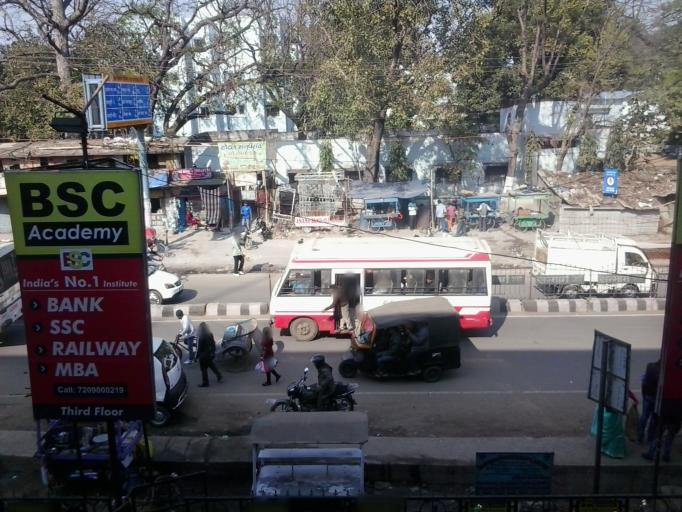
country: IN
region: Jharkhand
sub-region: Ranchi
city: Ranchi
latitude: 23.3800
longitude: 85.3146
